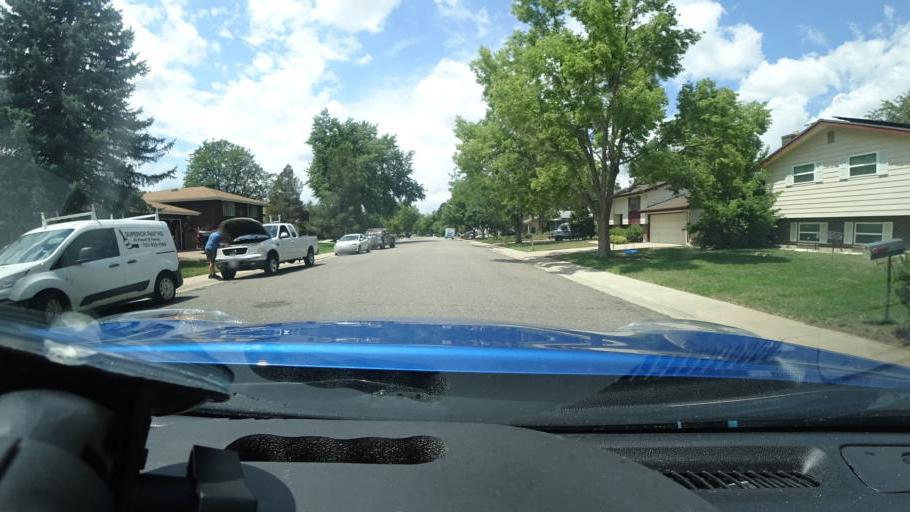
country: US
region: Colorado
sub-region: Adams County
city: Aurora
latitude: 39.7018
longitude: -104.8410
